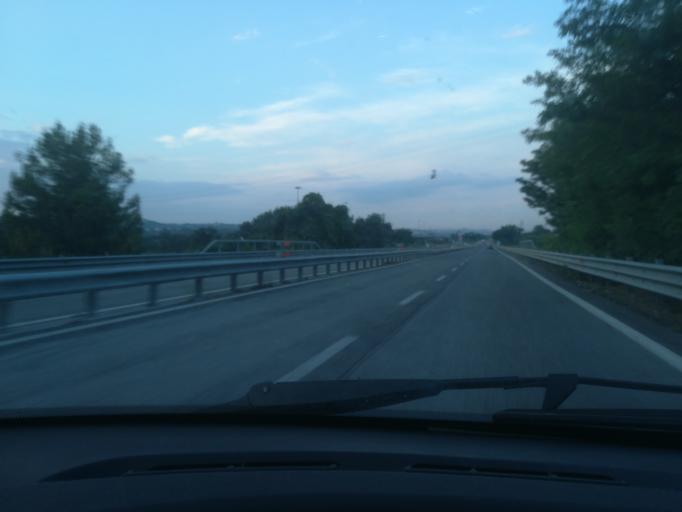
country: IT
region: The Marches
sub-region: Provincia di Macerata
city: Sforzacosta
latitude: 43.2494
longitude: 13.4357
